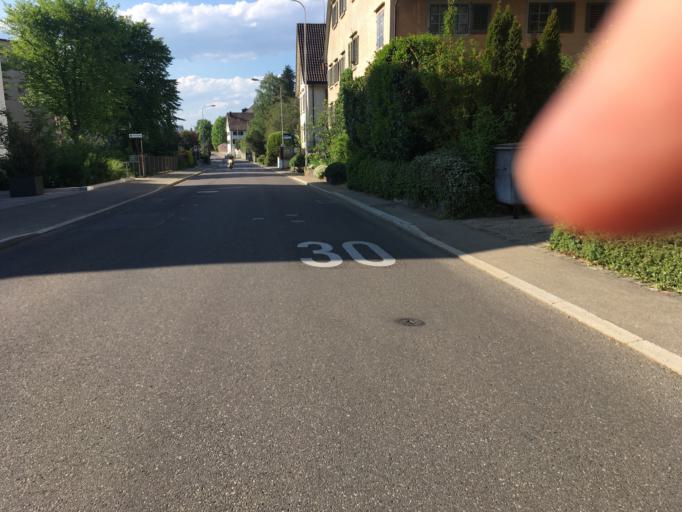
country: CH
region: Zurich
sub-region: Bezirk Meilen
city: Kuesnacht / Heslibach
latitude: 47.3130
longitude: 8.5890
